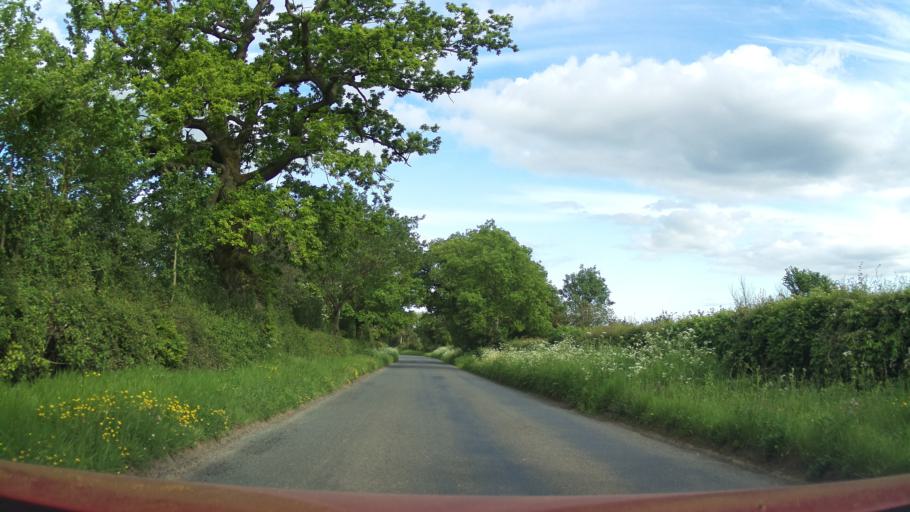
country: GB
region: England
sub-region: Gloucestershire
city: Moreton in Marsh
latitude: 52.0002
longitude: -1.7168
